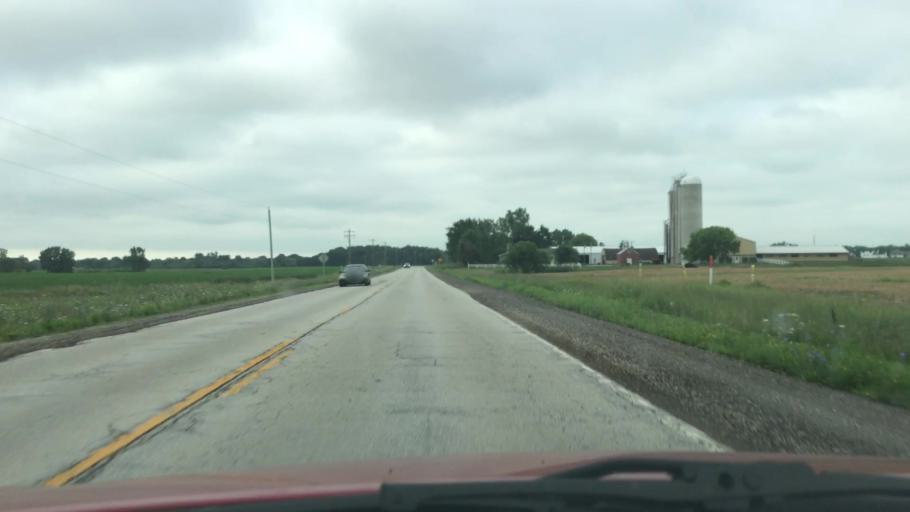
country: US
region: Wisconsin
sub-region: Brown County
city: De Pere
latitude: 44.4356
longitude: -88.1359
